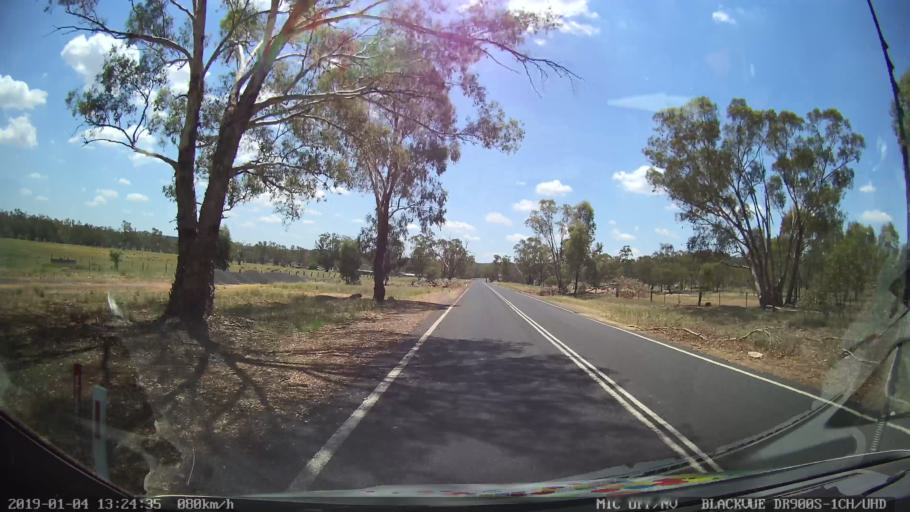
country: AU
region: New South Wales
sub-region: Parkes
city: Peak Hill
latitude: -32.7036
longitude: 148.5532
